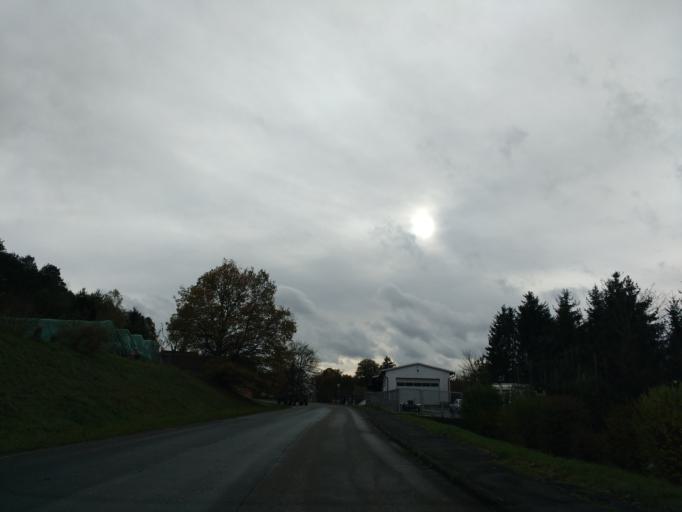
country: DE
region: Hesse
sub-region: Regierungsbezirk Kassel
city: Vohl
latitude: 51.2052
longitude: 8.9486
